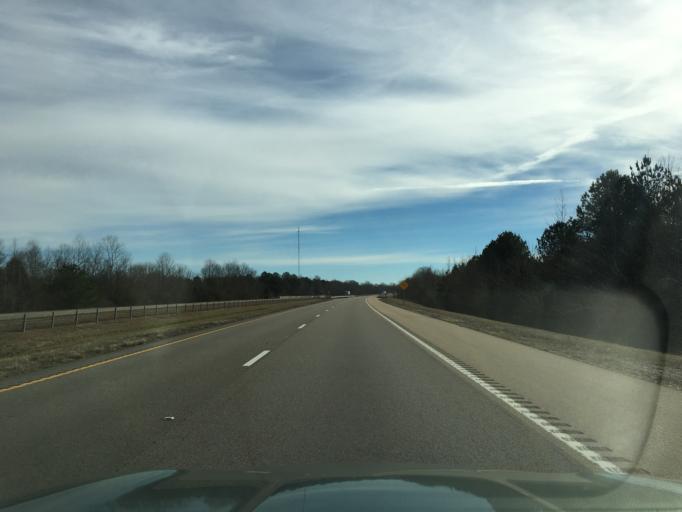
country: US
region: Mississippi
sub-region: Union County
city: New Albany
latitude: 34.5383
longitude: -89.0952
